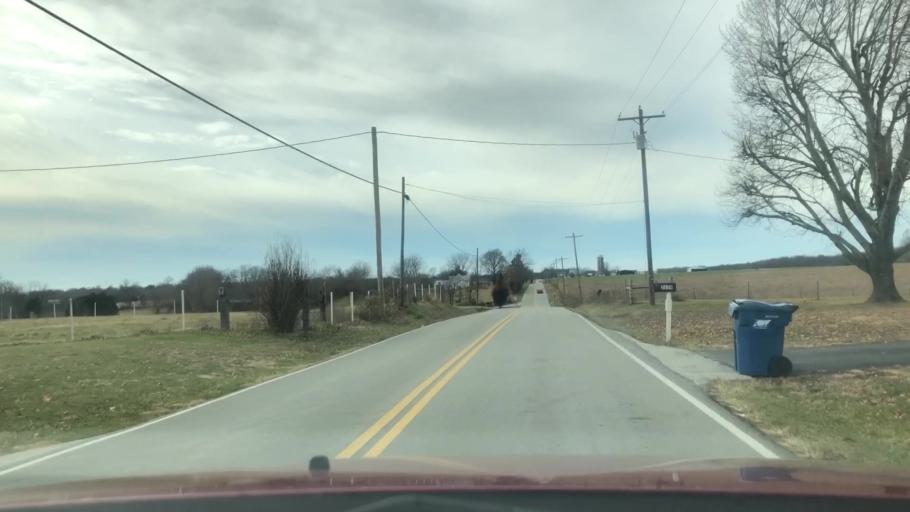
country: US
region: Missouri
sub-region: Greene County
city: Springfield
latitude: 37.2730
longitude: -93.2400
